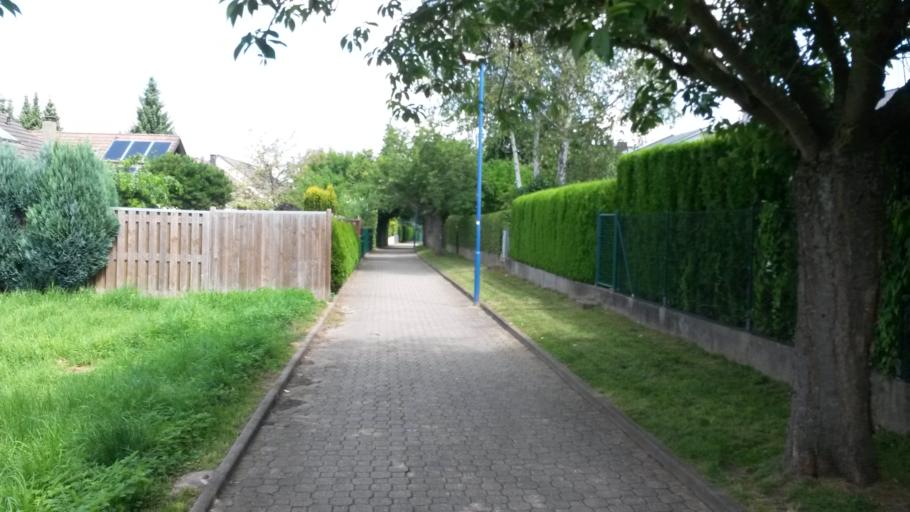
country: DE
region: Baden-Wuerttemberg
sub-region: Karlsruhe Region
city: Ettlingen
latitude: 48.9262
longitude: 8.4721
